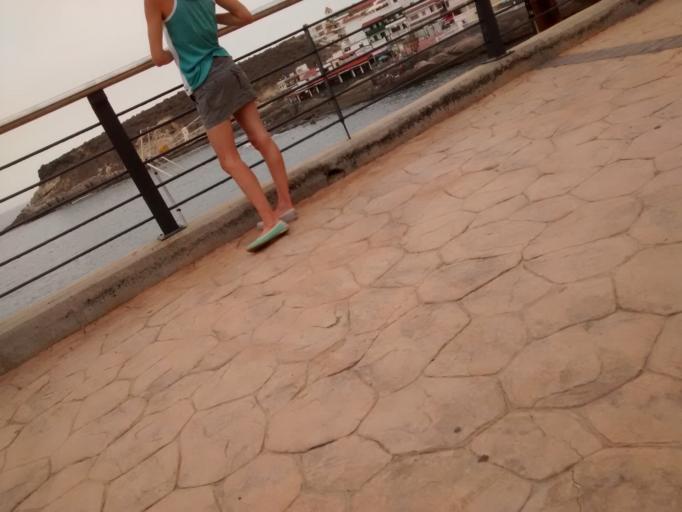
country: ES
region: Canary Islands
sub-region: Provincia de Santa Cruz de Tenerife
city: Adeje
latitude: 28.0999
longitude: -16.7555
